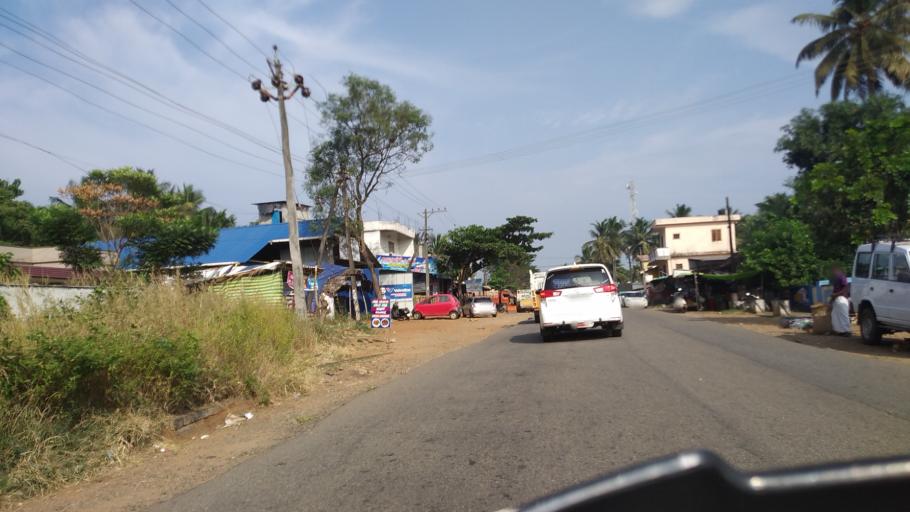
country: IN
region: Kerala
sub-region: Thrissur District
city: Chelakara
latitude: 10.5884
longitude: 76.5123
